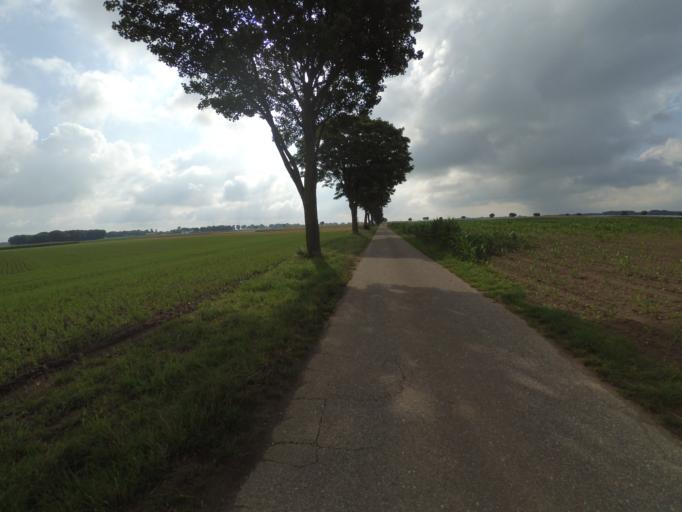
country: DE
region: North Rhine-Westphalia
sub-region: Regierungsbezirk Koln
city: Selfkant
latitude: 51.0482
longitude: 5.9157
